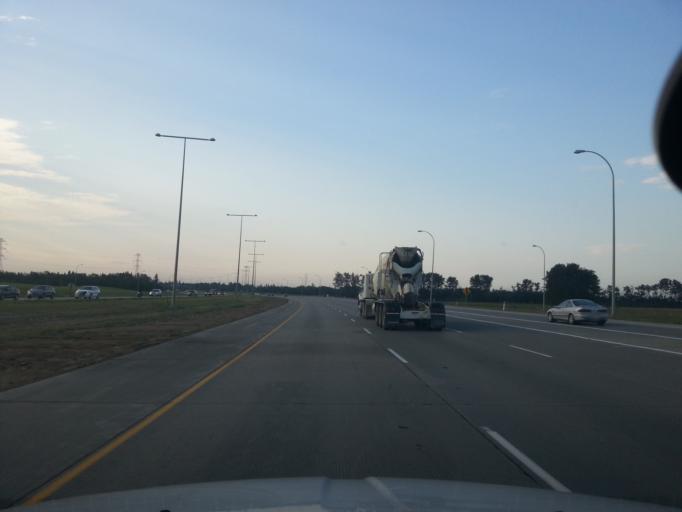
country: CA
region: Alberta
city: Devon
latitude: 53.4790
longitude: -113.6582
